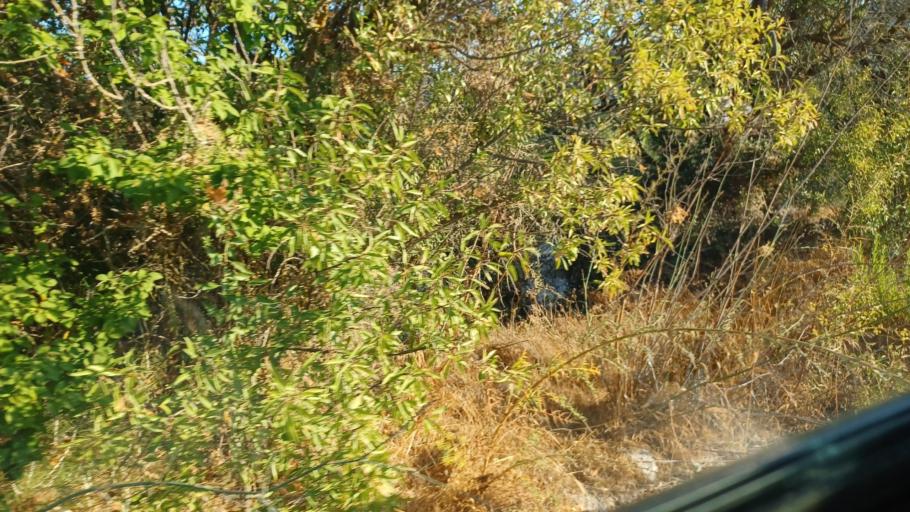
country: CY
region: Pafos
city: Mesogi
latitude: 34.8668
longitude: 32.4911
